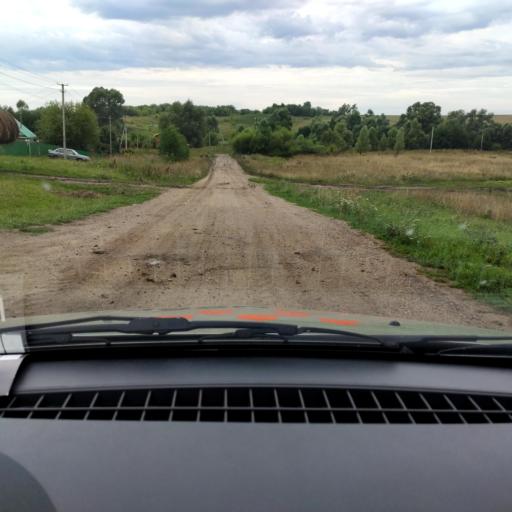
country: RU
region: Bashkortostan
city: Kabakovo
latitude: 54.5869
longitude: 56.2691
